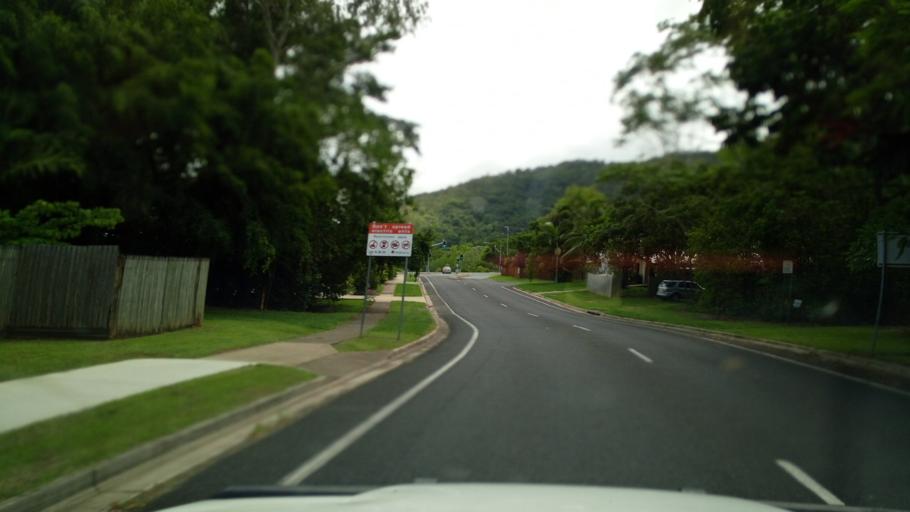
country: AU
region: Queensland
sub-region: Cairns
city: Yorkeys Knob
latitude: -16.8373
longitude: 145.6892
